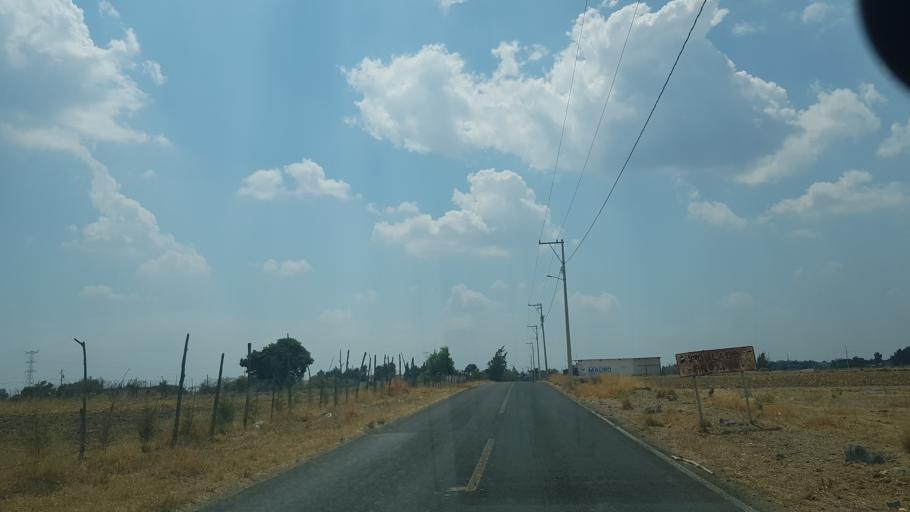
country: MX
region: Puebla
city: San Juan Amecac
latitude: 18.8283
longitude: -98.6509
